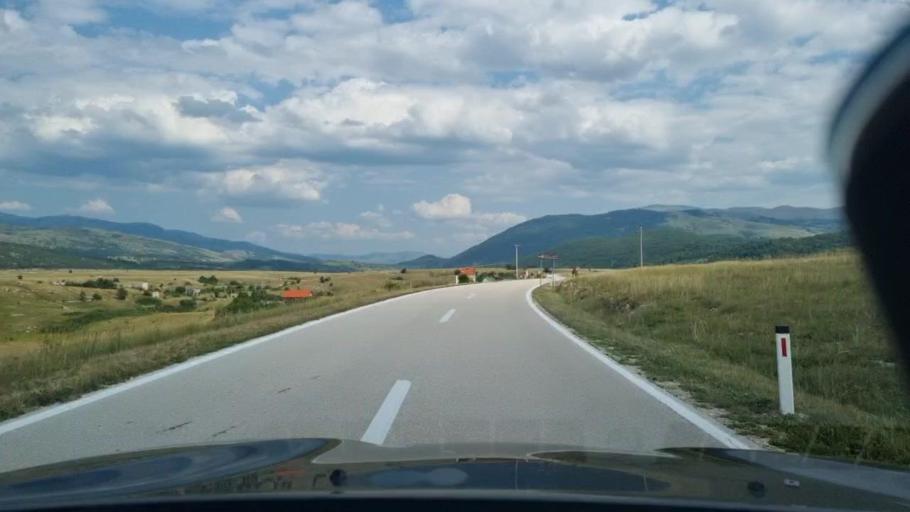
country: BA
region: Federation of Bosnia and Herzegovina
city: Bosansko Grahovo
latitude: 44.1545
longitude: 16.4352
